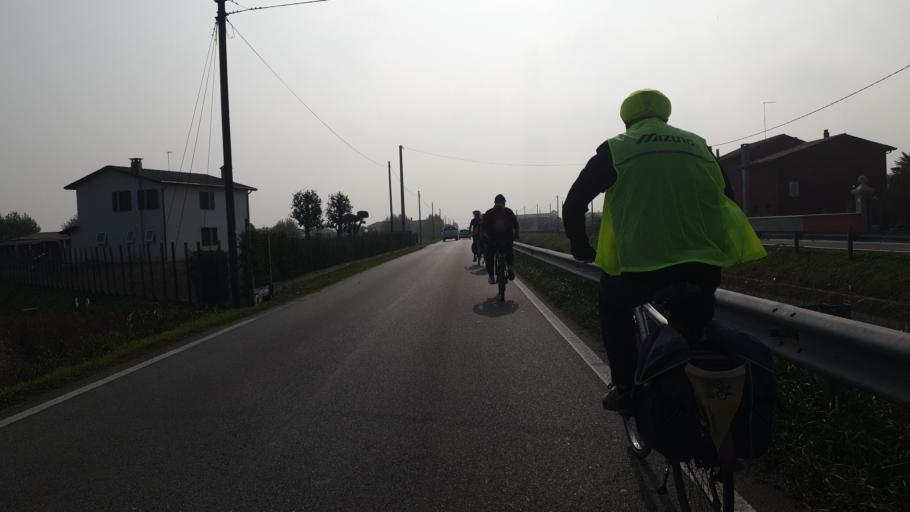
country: IT
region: Veneto
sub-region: Provincia di Padova
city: Corte
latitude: 45.3016
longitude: 12.0782
